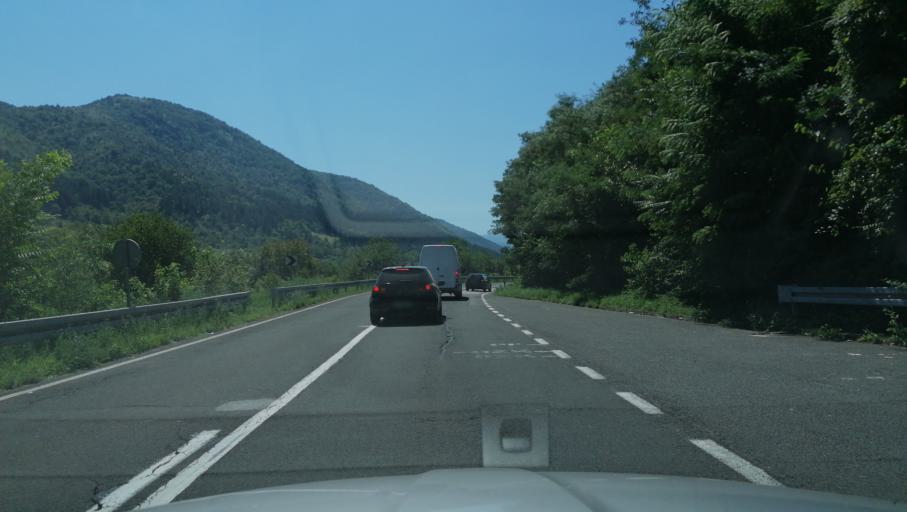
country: RS
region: Central Serbia
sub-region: Raski Okrug
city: Kraljevo
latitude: 43.6568
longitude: 20.5613
